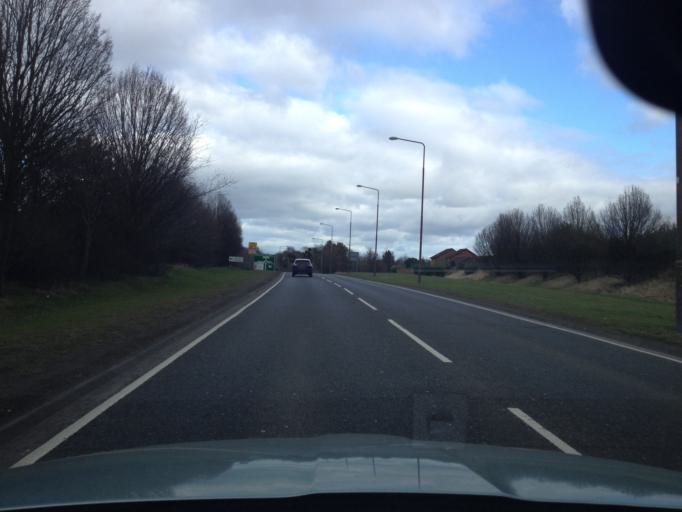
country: GB
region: Scotland
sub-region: West Lothian
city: Mid Calder
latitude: 55.8793
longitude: -3.4956
